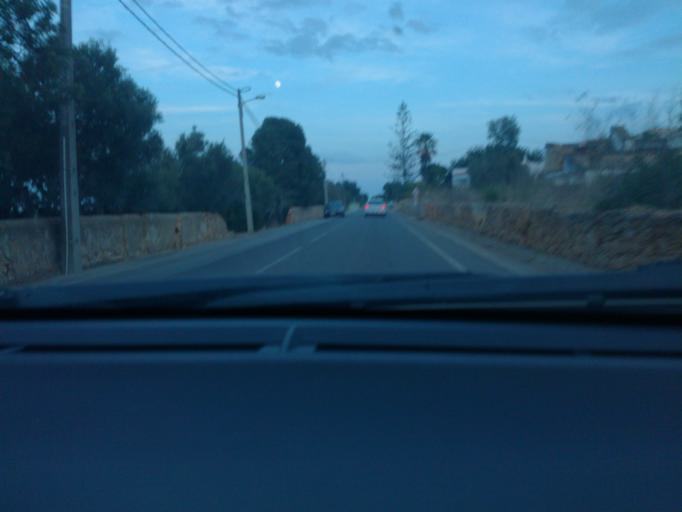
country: PT
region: Faro
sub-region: Olhao
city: Laranjeiro
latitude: 37.0622
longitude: -7.7571
